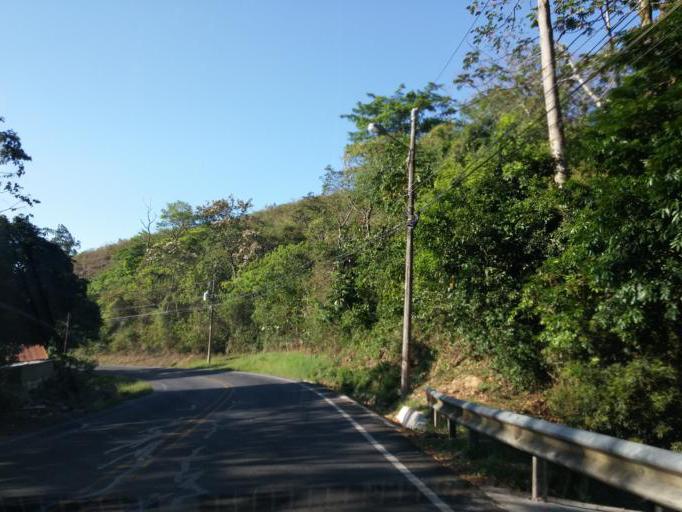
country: CR
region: Heredia
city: Colon
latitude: 9.8903
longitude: -84.2267
